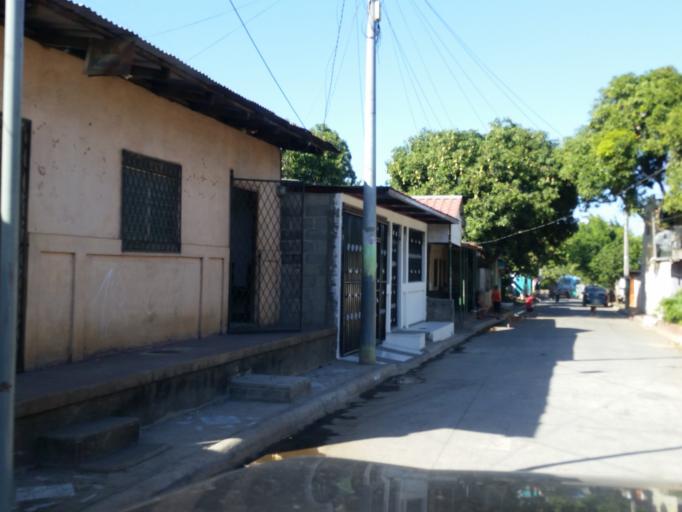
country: NI
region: Managua
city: Managua
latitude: 12.1262
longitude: -86.2798
